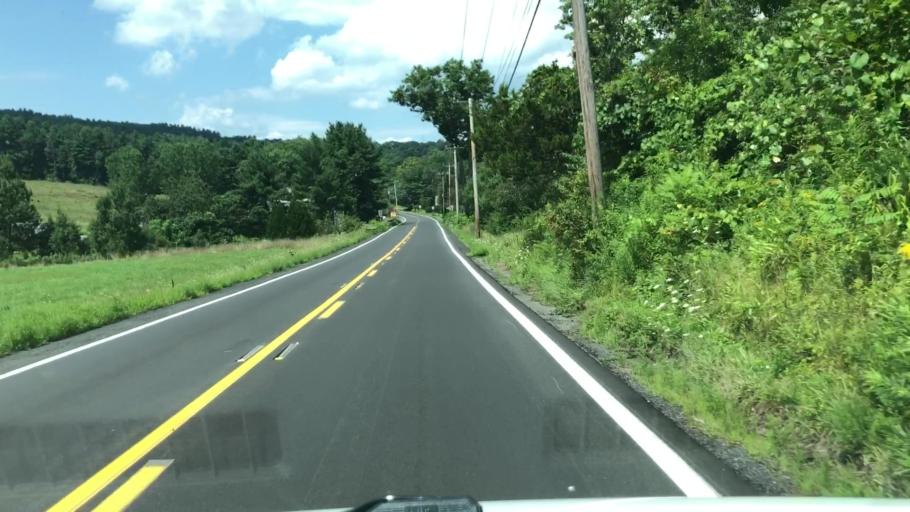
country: US
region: Massachusetts
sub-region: Franklin County
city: Ashfield
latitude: 42.5162
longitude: -72.7778
